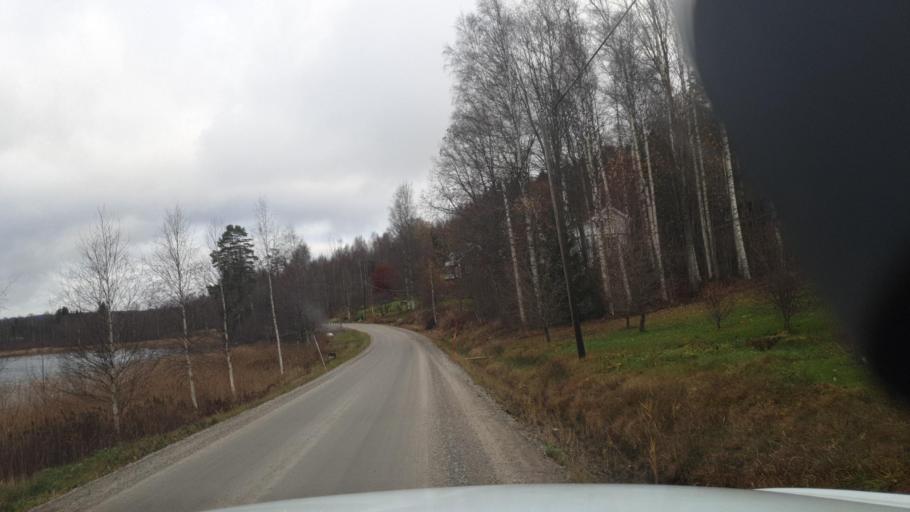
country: SE
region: Vaermland
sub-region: Arvika Kommun
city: Arvika
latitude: 59.7427
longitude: 12.8304
